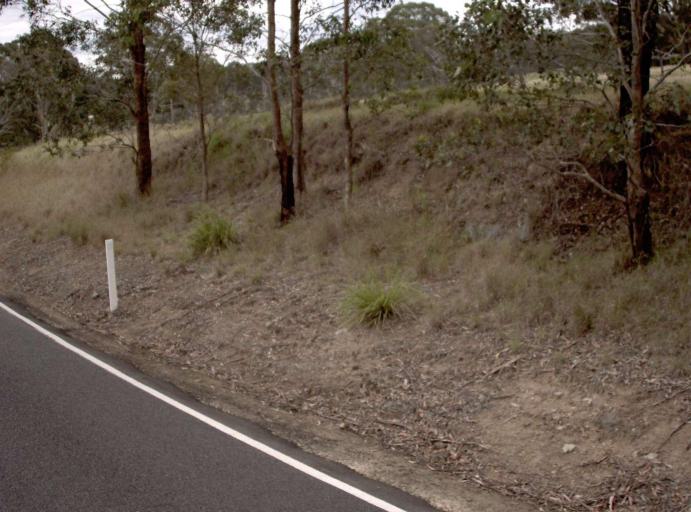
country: AU
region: New South Wales
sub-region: Bombala
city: Bombala
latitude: -37.4833
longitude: 149.1801
